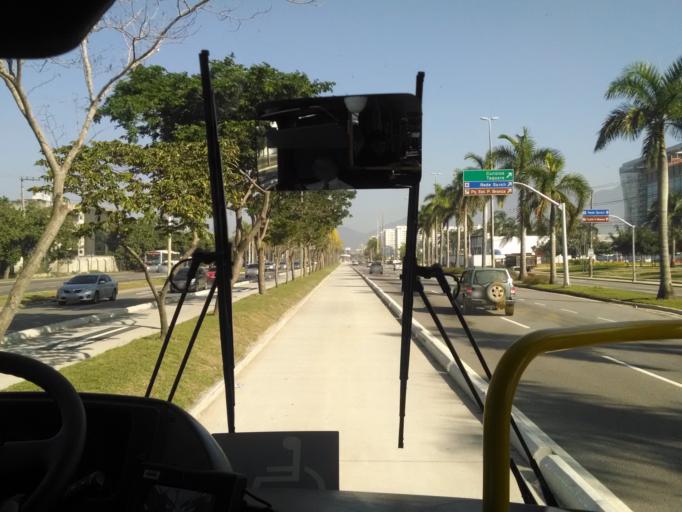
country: BR
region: Rio de Janeiro
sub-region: Sao Joao De Meriti
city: Sao Joao de Meriti
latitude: -22.9733
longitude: -43.3727
